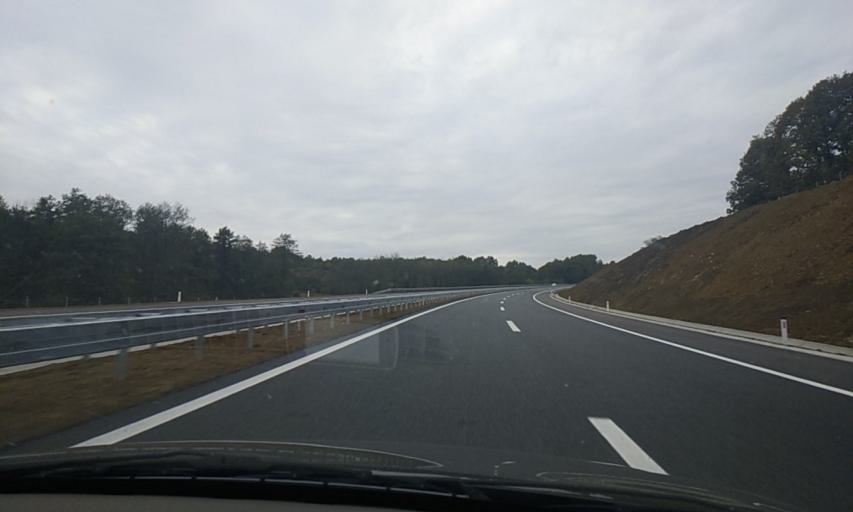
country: BA
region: Republika Srpska
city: Prnjavor
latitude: 44.8687
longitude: 17.5240
